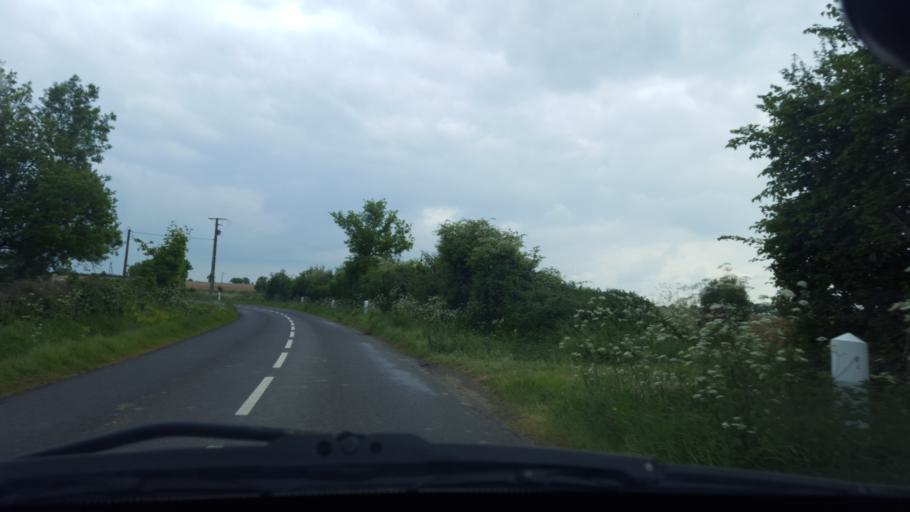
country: FR
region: Pays de la Loire
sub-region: Departement de la Loire-Atlantique
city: La Limouziniere
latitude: 47.0041
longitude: -1.6160
